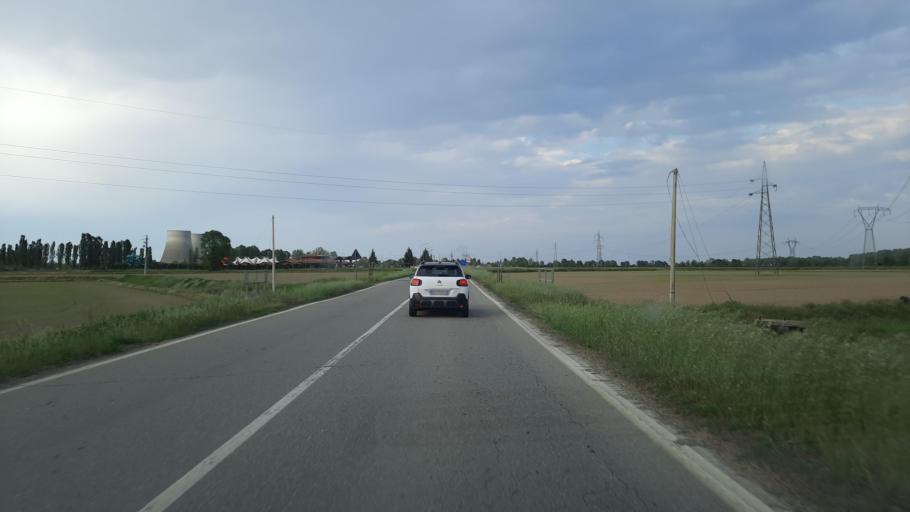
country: IT
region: Piedmont
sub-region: Provincia di Vercelli
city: Fontanetto Po
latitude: 45.2391
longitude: 8.1766
